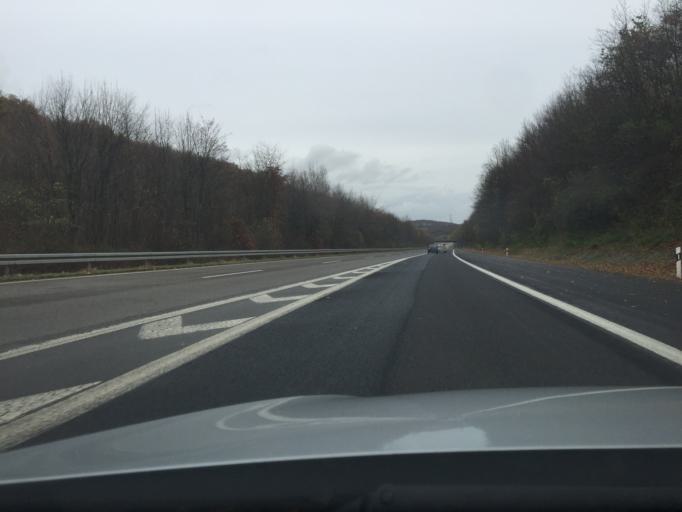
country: DE
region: North Rhine-Westphalia
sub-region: Regierungsbezirk Dusseldorf
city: Velbert
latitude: 51.3550
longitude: 7.0454
